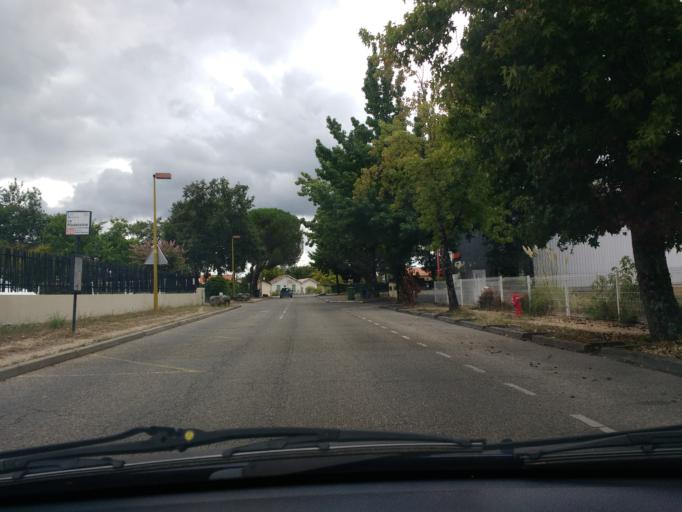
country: FR
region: Aquitaine
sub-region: Departement de la Gironde
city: Canejan
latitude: 44.7746
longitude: -0.6372
